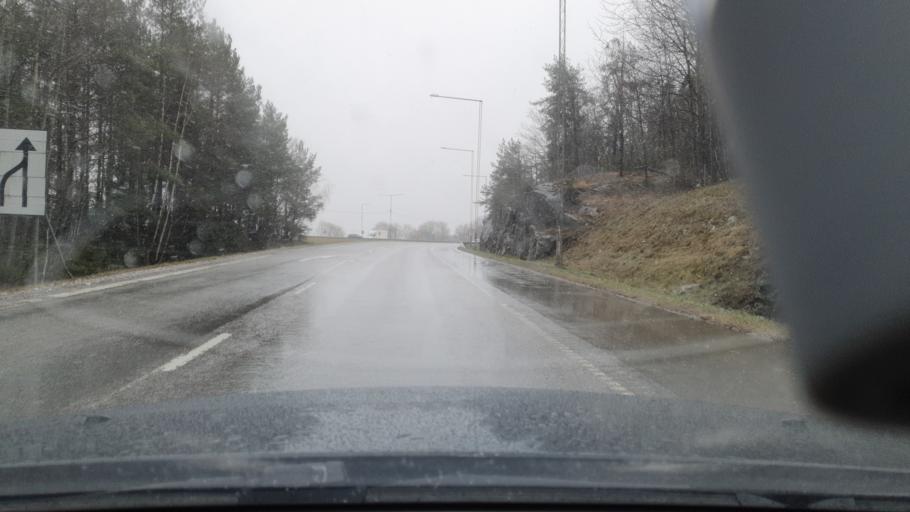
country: SE
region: Stockholm
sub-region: Jarfalla Kommun
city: Jakobsberg
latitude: 59.4206
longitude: 17.8500
